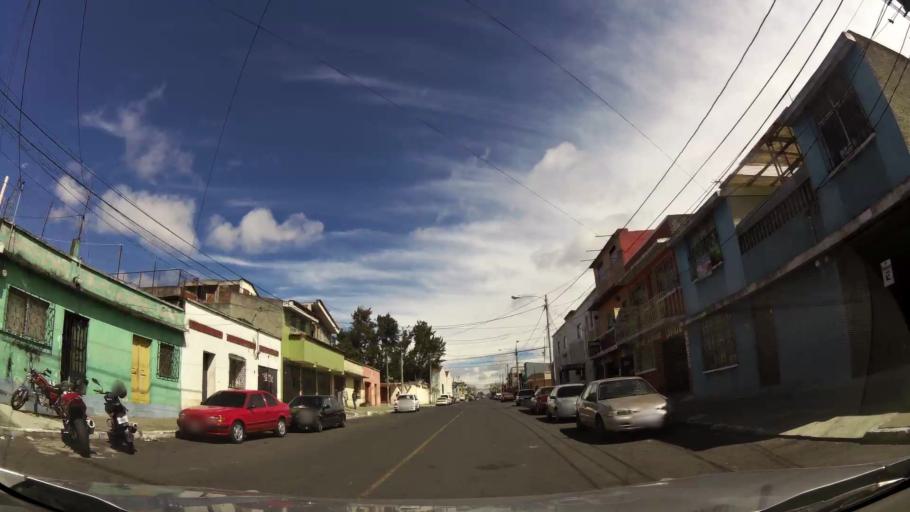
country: GT
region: Guatemala
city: Guatemala City
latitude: 14.6036
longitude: -90.5392
